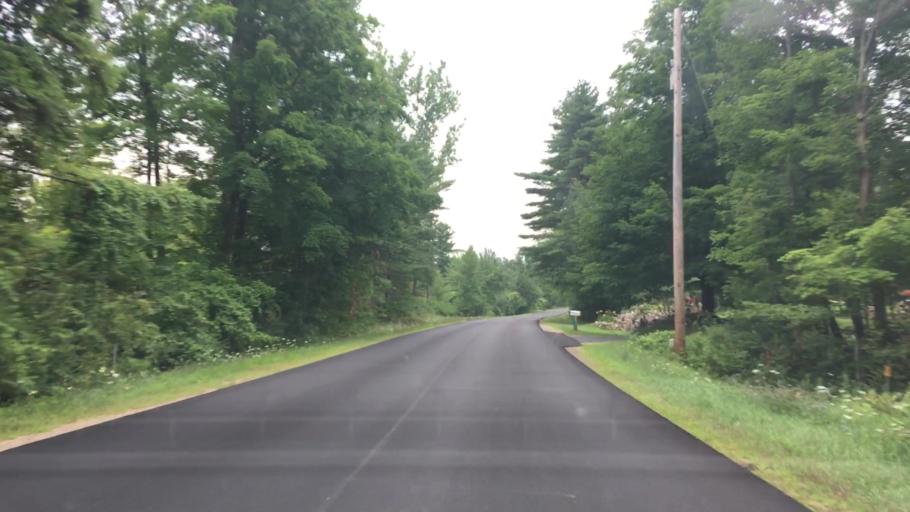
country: US
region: New York
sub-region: Clinton County
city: Peru
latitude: 44.5797
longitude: -73.5699
